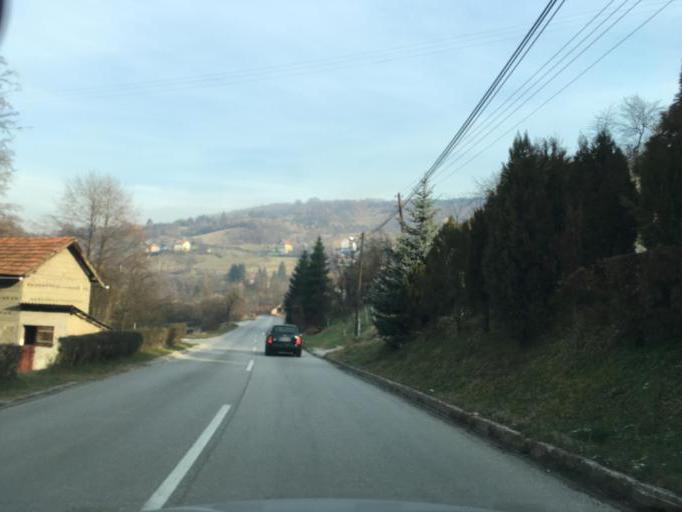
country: BA
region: Federation of Bosnia and Herzegovina
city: Lokvine
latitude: 44.1927
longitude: 17.8731
